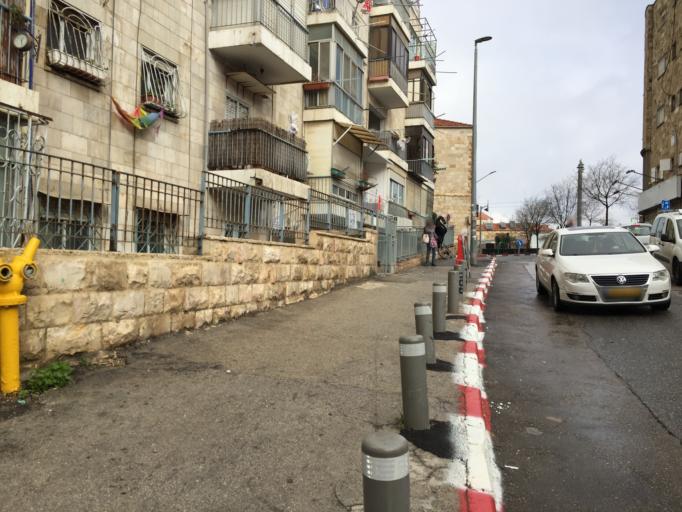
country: IL
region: Jerusalem
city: West Jerusalem
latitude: 31.7856
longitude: 35.2104
